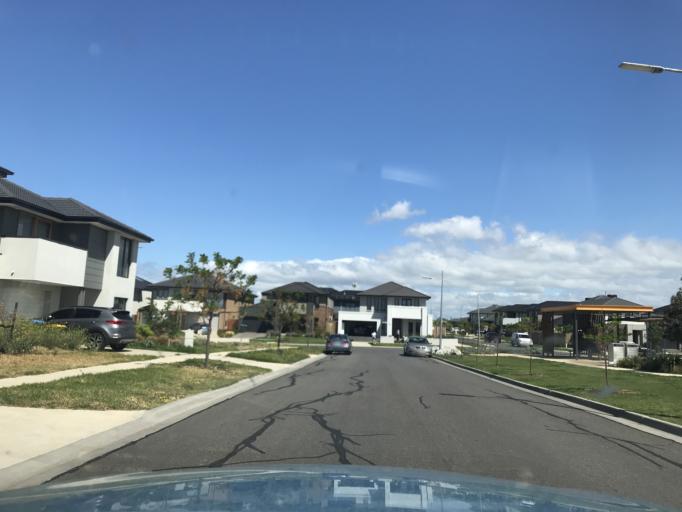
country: AU
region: Victoria
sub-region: Wyndham
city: Williams Landing
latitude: -37.8645
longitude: 144.7360
